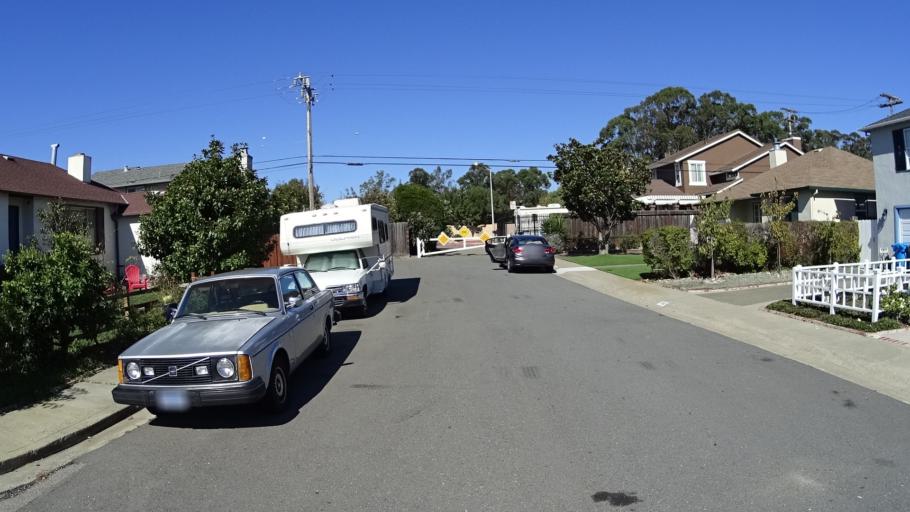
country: US
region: California
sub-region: San Mateo County
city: San Bruno
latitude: 37.6268
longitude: -122.4202
